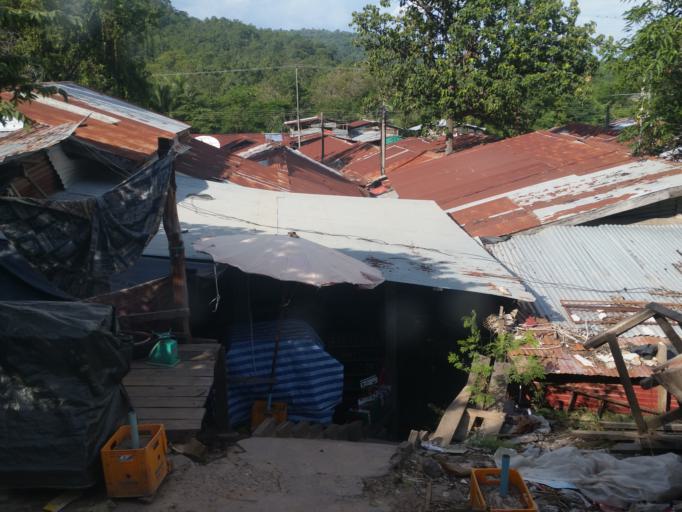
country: TH
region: Changwat Ubon Ratchathani
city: Sirindhorn
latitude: 15.1311
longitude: 105.4696
